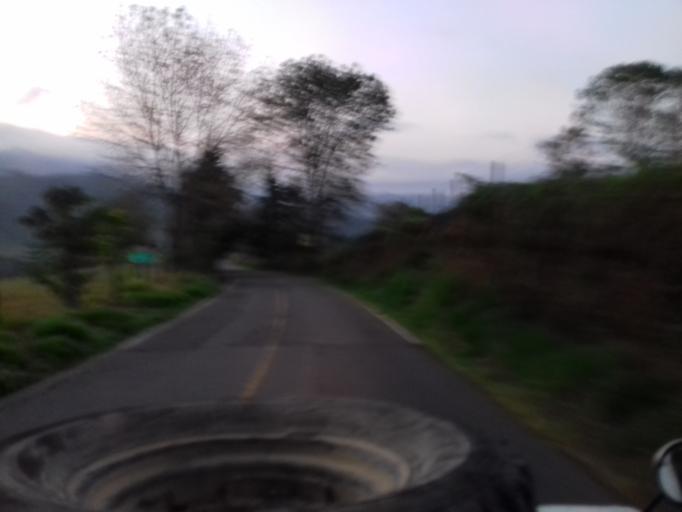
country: CO
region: Quindio
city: Salento
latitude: 4.6486
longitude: -75.5896
